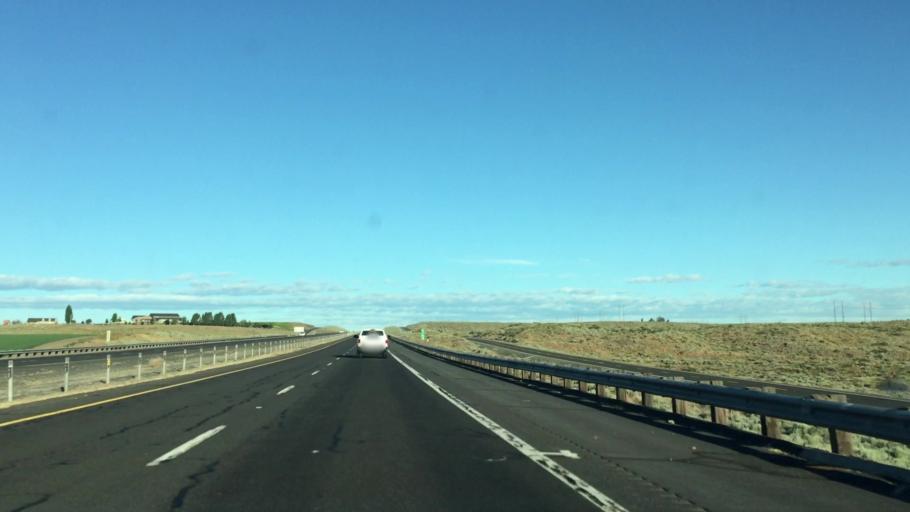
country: US
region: Washington
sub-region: Grant County
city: Cascade Valley
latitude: 47.1042
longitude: -119.4622
